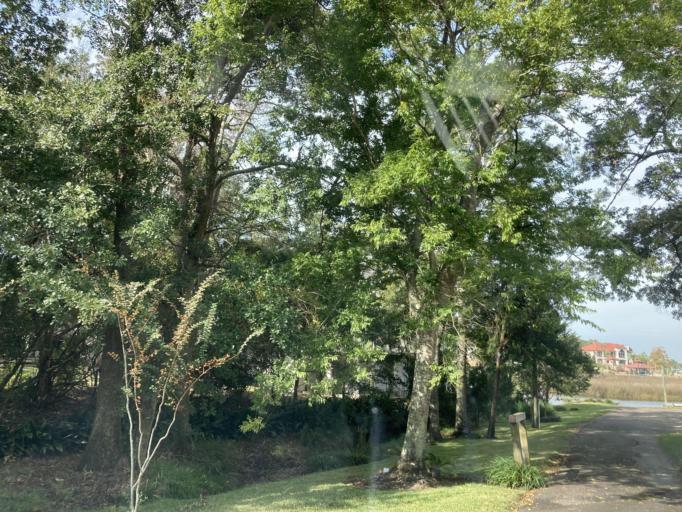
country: US
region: Mississippi
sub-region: Jackson County
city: Ocean Springs
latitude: 30.4173
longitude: -88.8314
